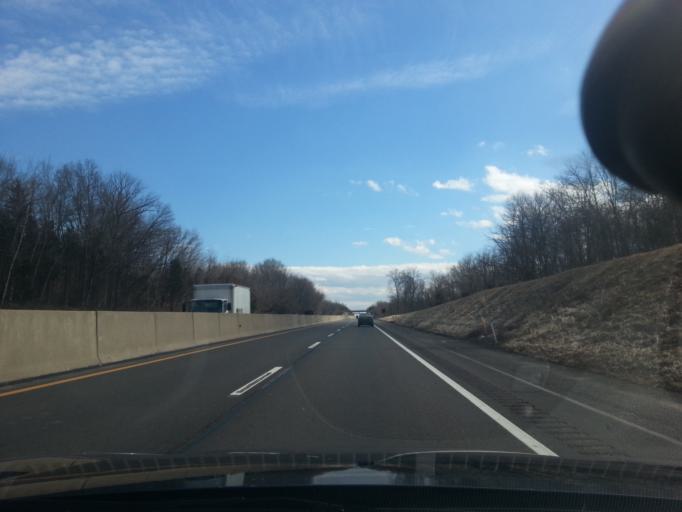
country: US
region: Pennsylvania
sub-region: Montgomery County
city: Woxall
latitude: 40.3610
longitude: -75.3966
